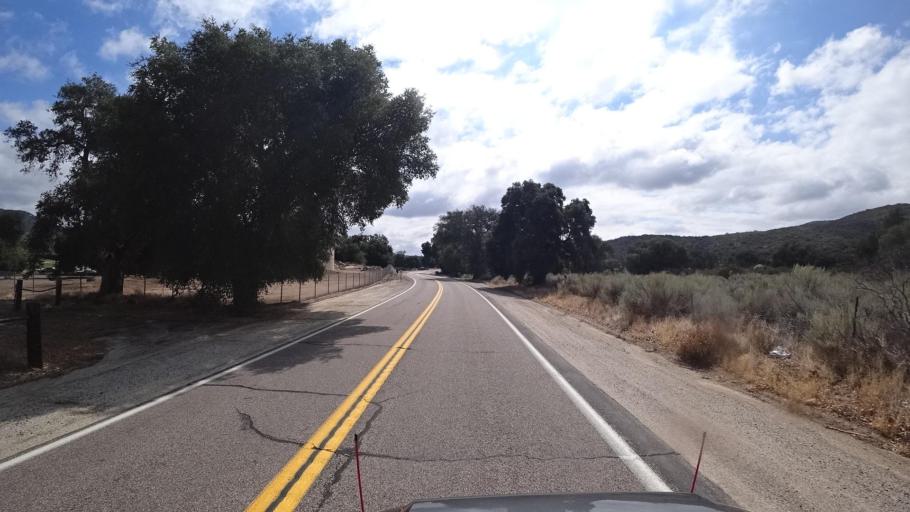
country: US
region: California
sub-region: San Diego County
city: Pine Valley
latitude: 32.7361
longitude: -116.4939
